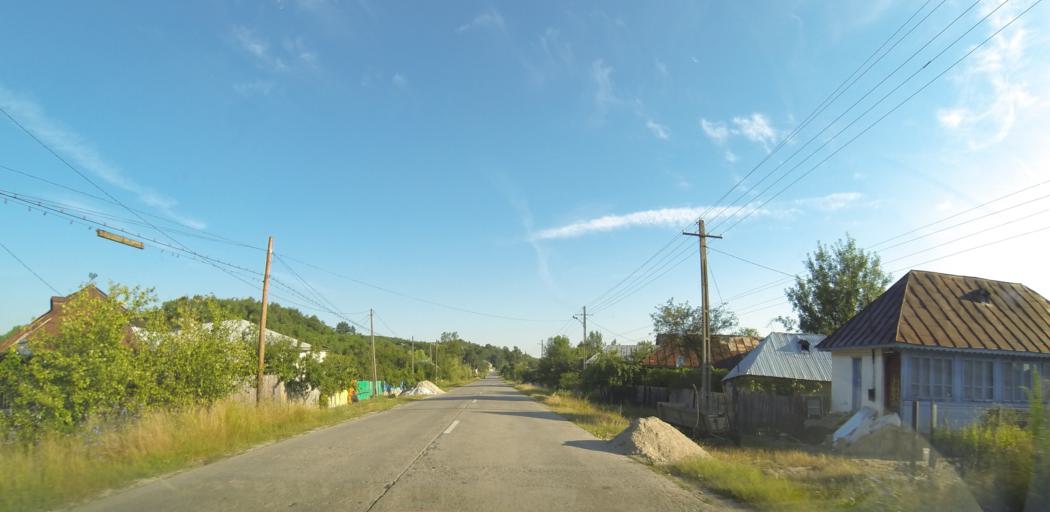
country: RO
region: Dolj
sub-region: Comuna Bulzesti
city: Bulzesti
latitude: 44.5210
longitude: 23.8967
